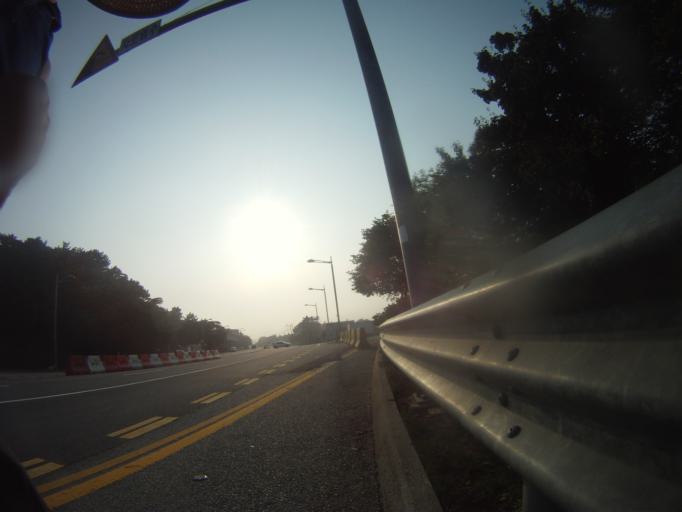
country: KR
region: Incheon
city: Incheon
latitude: 37.4222
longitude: 126.4367
